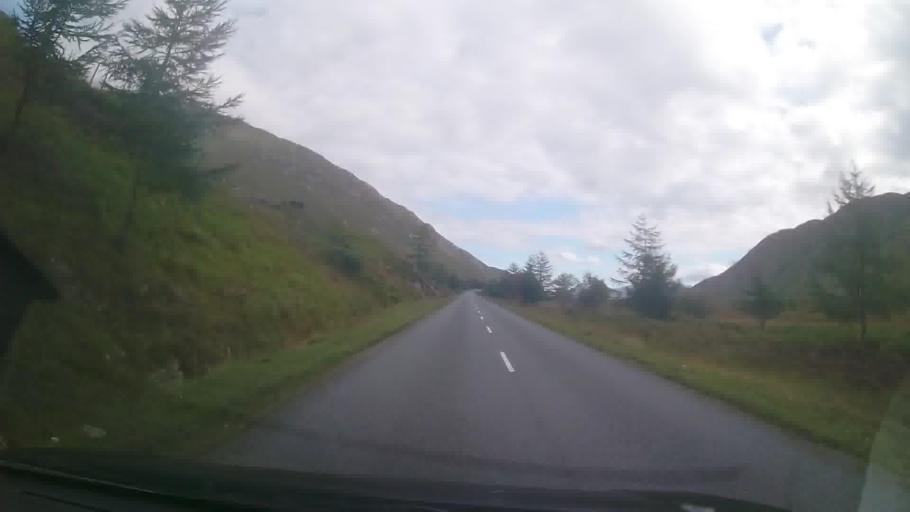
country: GB
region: Scotland
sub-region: Argyll and Bute
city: Oban
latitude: 56.6875
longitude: -5.4439
